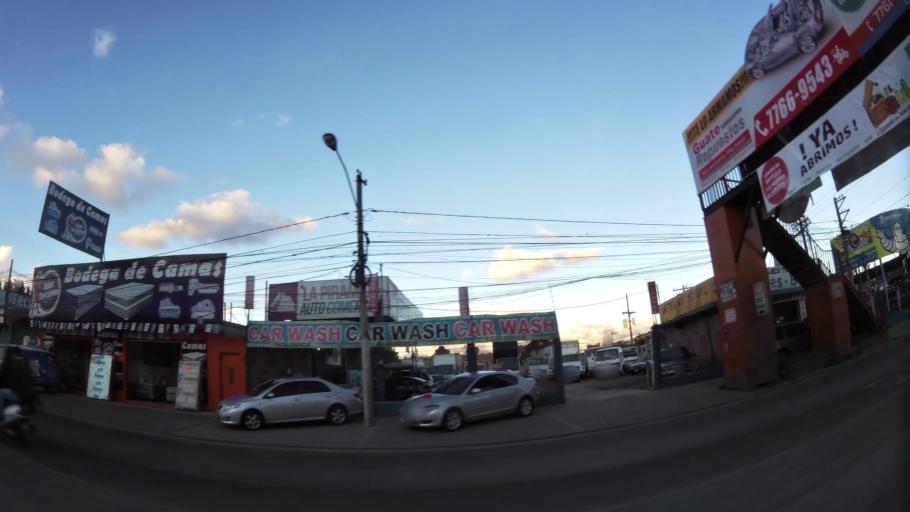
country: GT
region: Quetzaltenango
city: Quetzaltenango
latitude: 14.8409
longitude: -91.5102
